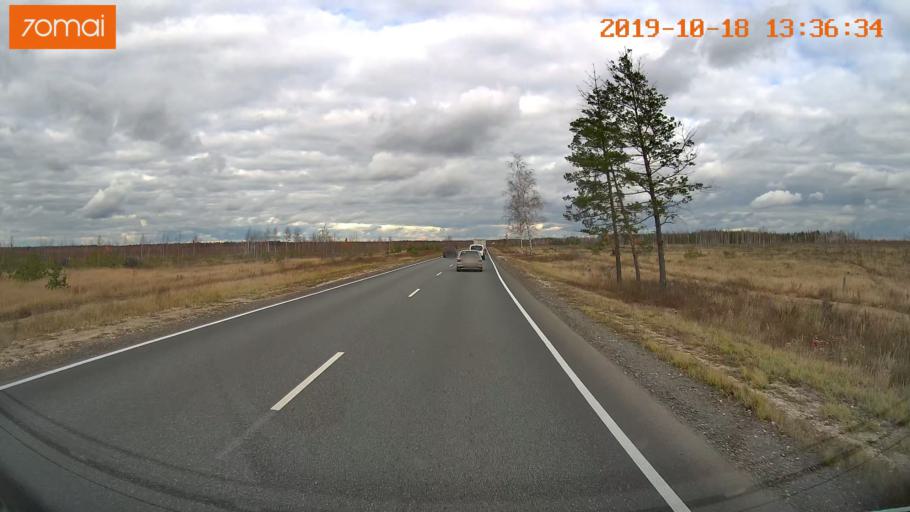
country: RU
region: Rjazan
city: Solotcha
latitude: 54.8717
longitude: 39.9854
